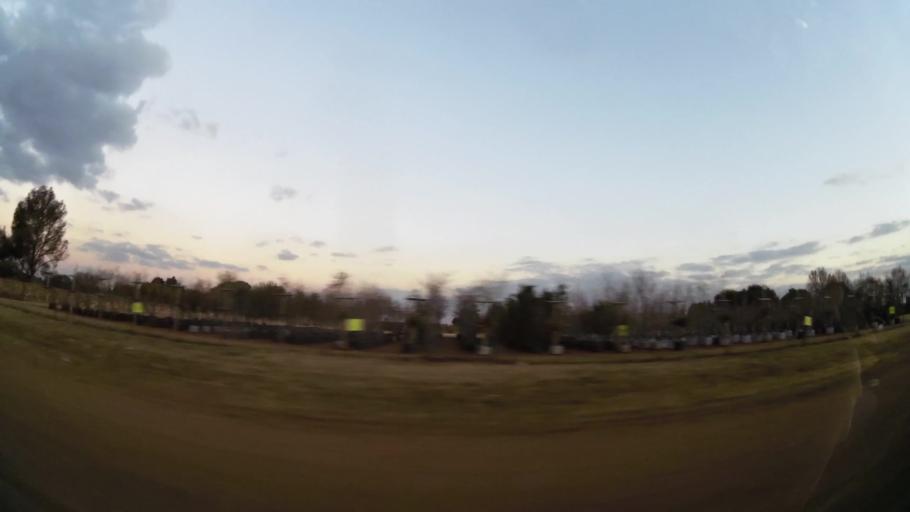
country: ZA
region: Gauteng
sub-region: West Rand District Municipality
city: Krugersdorp
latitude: -26.0714
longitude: 27.6670
